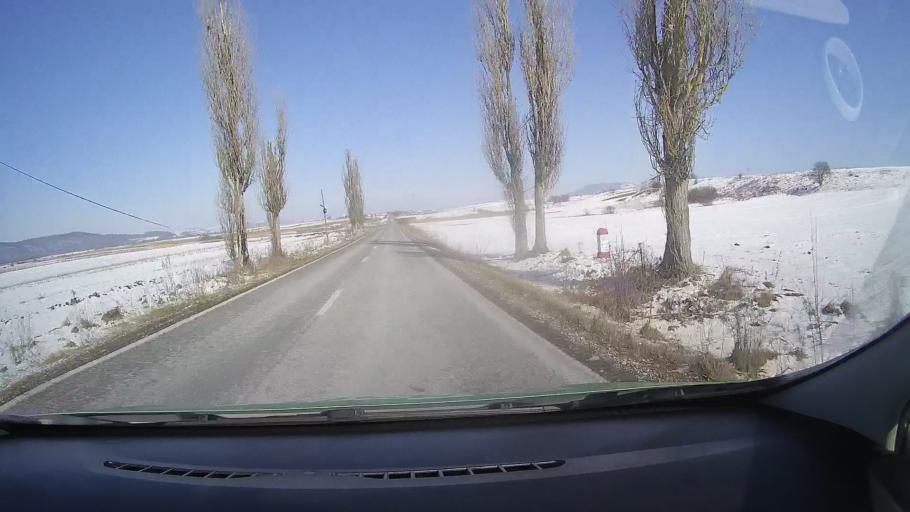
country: RO
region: Brasov
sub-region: Comuna Parau
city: Parau
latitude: 45.8622
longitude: 25.1994
